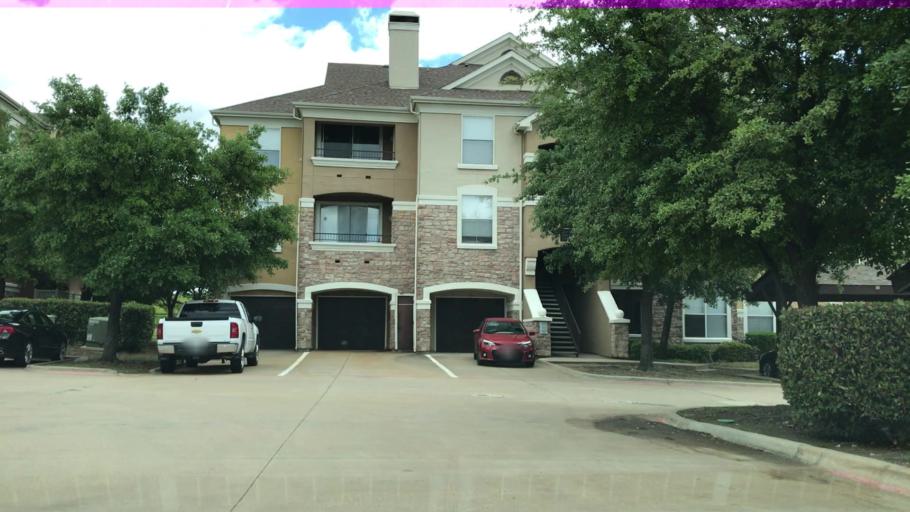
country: US
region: Texas
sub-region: Dallas County
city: Farmers Branch
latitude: 32.8912
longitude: -96.9561
